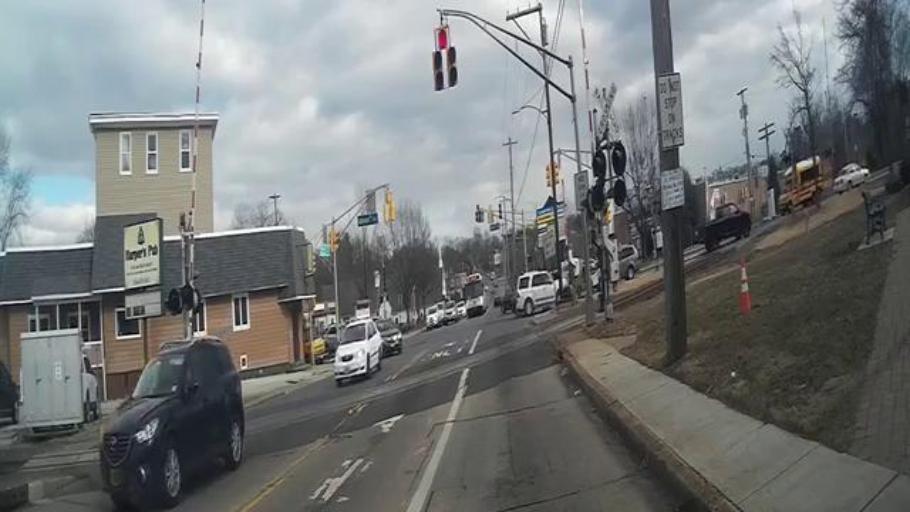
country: US
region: New Jersey
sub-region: Camden County
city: Clementon
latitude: 39.8056
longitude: -74.9908
